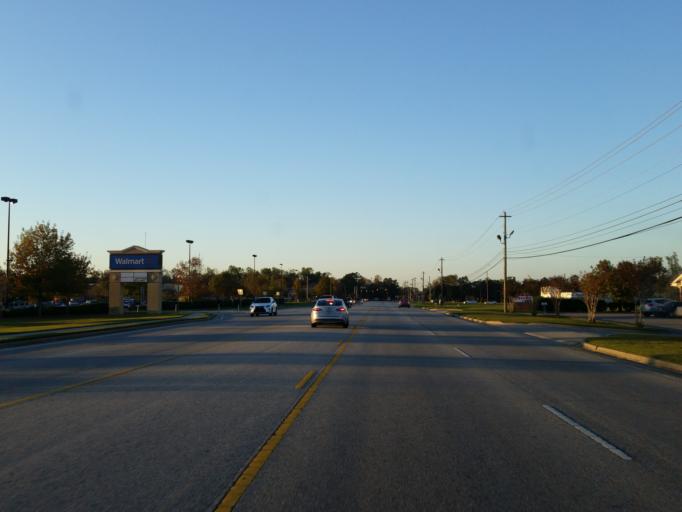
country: US
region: Georgia
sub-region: Lowndes County
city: Remerton
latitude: 30.8261
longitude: -83.3172
